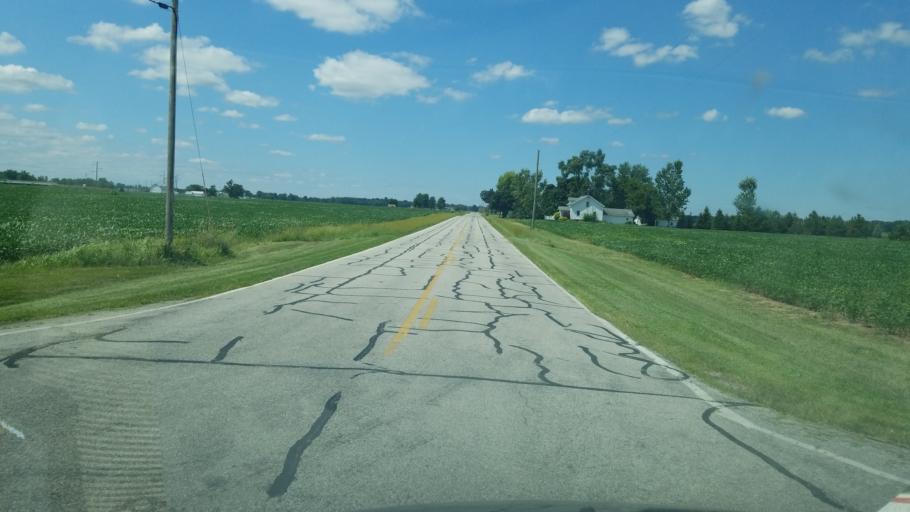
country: US
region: Ohio
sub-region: Fulton County
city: Delta
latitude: 41.6032
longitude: -83.9988
